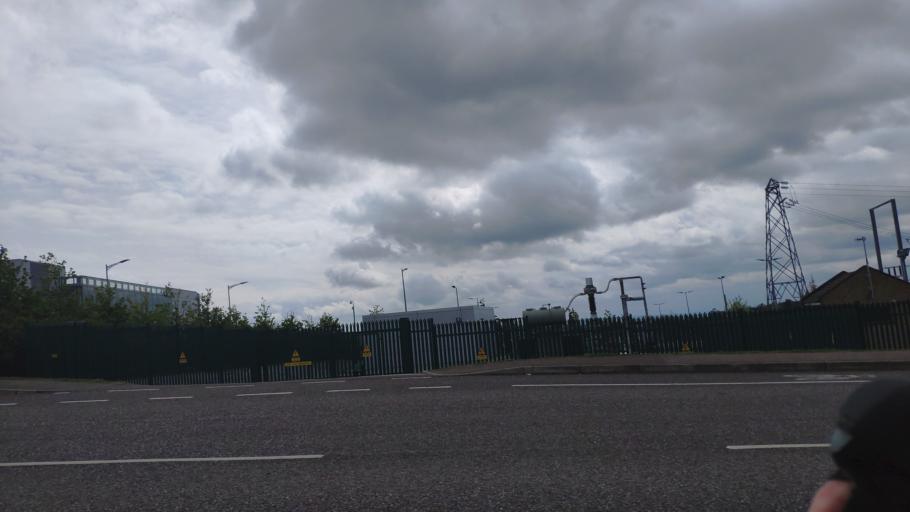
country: IE
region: Munster
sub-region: County Cork
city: Cork
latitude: 51.9076
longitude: -8.5118
